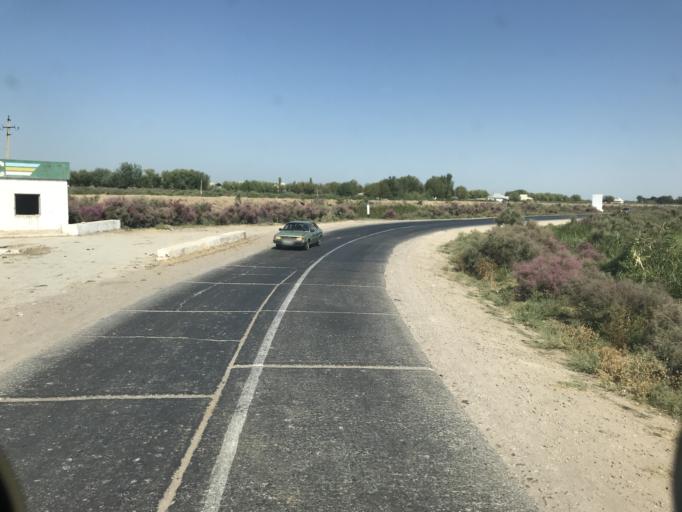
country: KZ
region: Ongtustik Qazaqstan
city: Myrzakent
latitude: 40.7497
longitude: 68.5372
